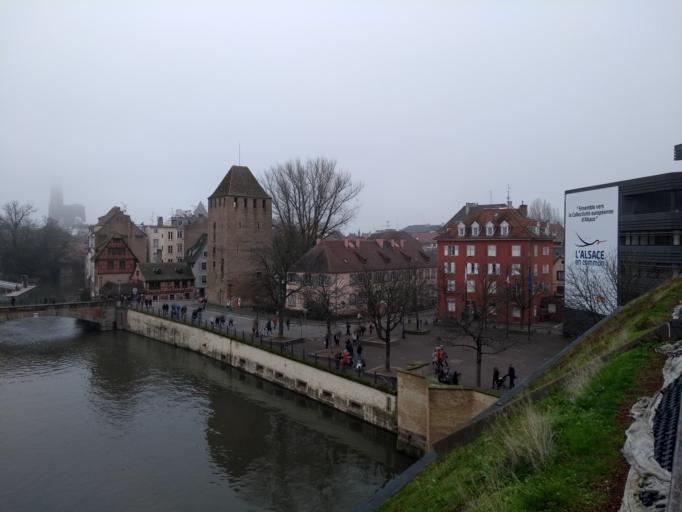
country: FR
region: Alsace
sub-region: Departement du Bas-Rhin
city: Strasbourg
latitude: 48.5795
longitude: 7.7383
